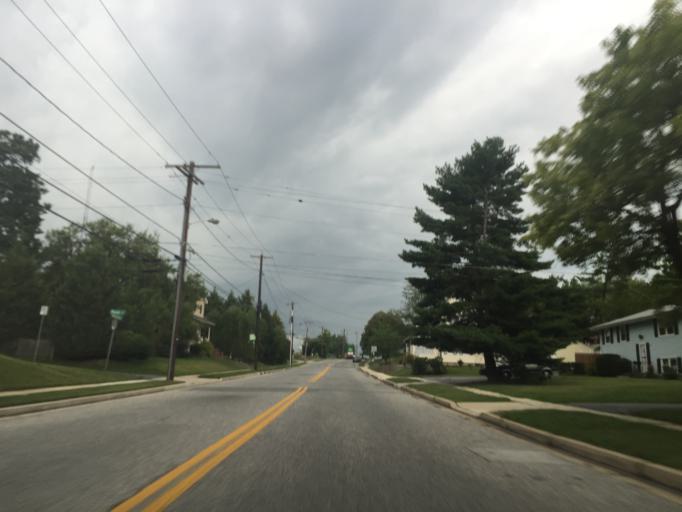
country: US
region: Maryland
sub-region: Baltimore County
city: Parkville
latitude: 39.3856
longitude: -76.5442
